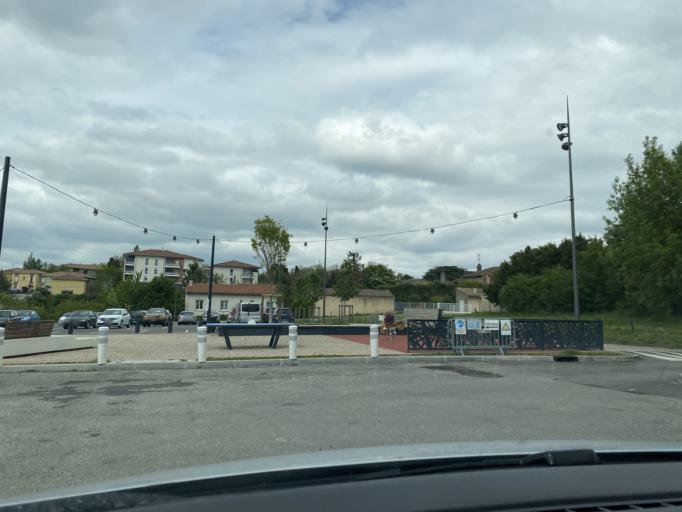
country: FR
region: Midi-Pyrenees
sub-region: Departement de la Haute-Garonne
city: Nailloux
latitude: 43.3584
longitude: 1.6225
